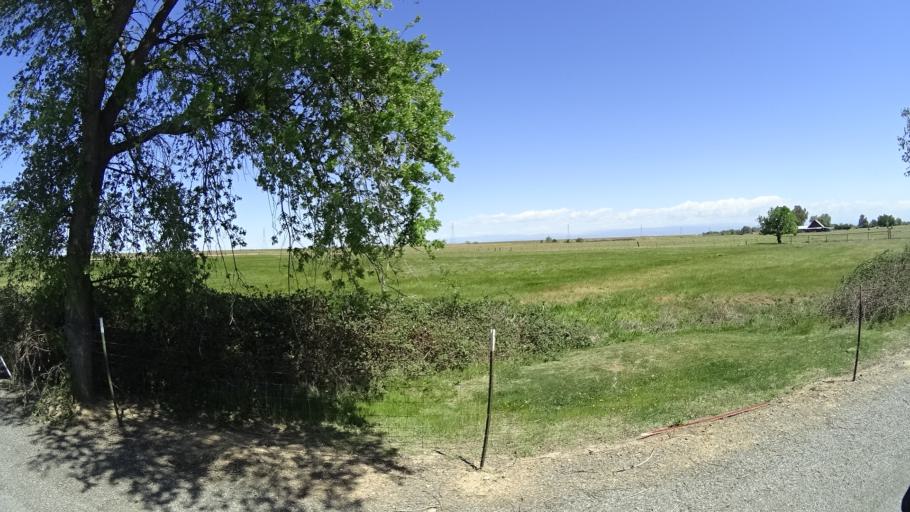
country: US
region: California
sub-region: Glenn County
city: Orland
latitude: 39.7946
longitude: -122.2264
